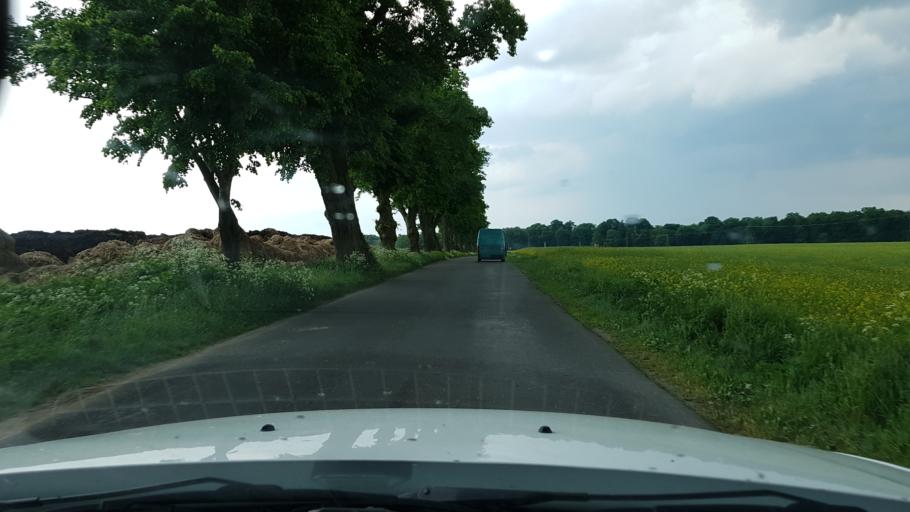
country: PL
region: West Pomeranian Voivodeship
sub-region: Powiat stargardzki
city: Dolice
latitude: 53.3064
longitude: 15.1754
